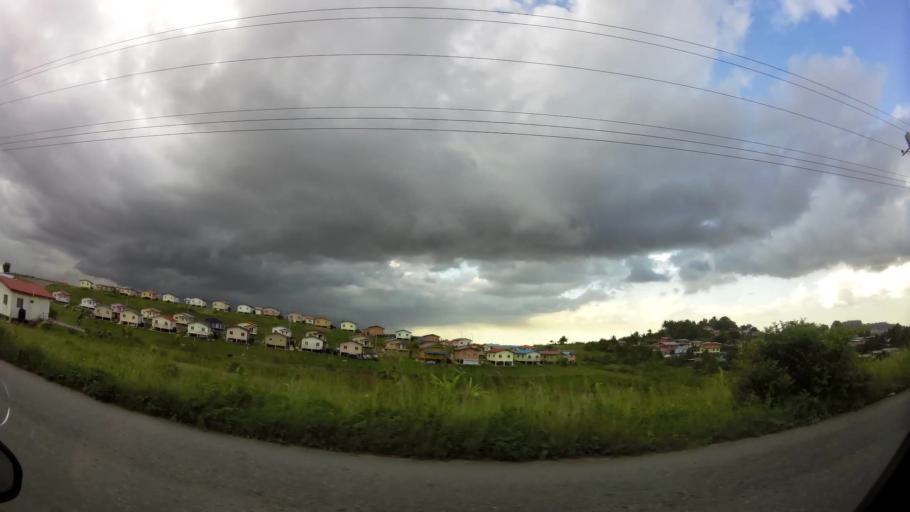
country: TT
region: City of San Fernando
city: Mon Repos
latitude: 10.2473
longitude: -61.4372
